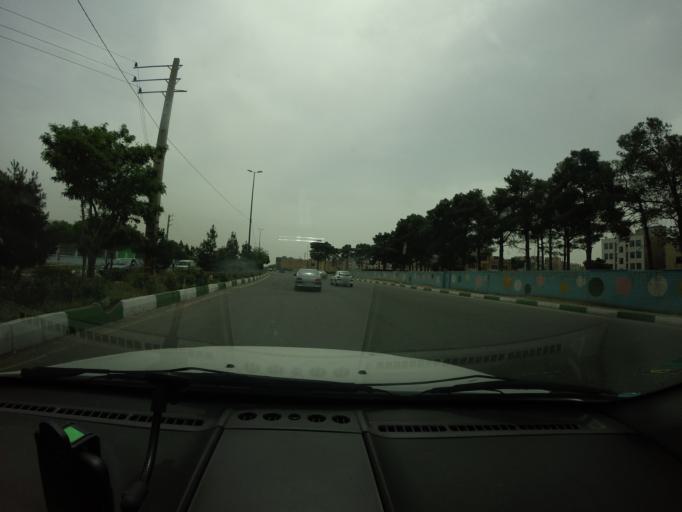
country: IR
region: Tehran
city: Eslamshahr
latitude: 35.5394
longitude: 51.2216
